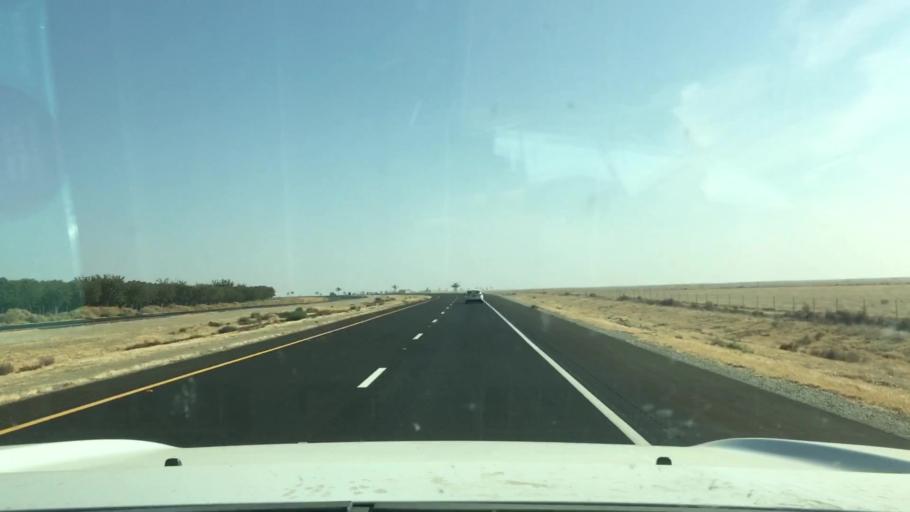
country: US
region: California
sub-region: Kern County
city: Lost Hills
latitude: 35.6160
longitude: -119.9681
